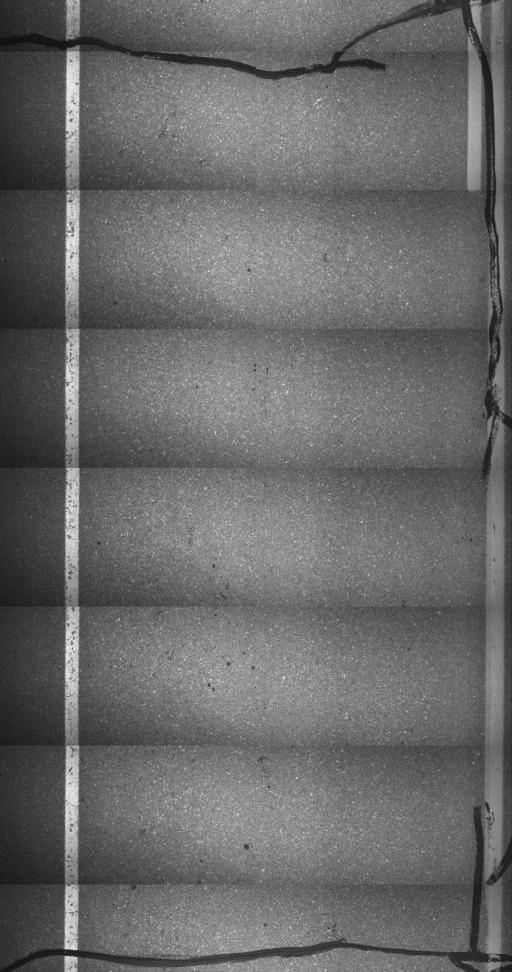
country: US
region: Vermont
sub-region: Orleans County
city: Newport
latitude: 44.9714
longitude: -72.3194
